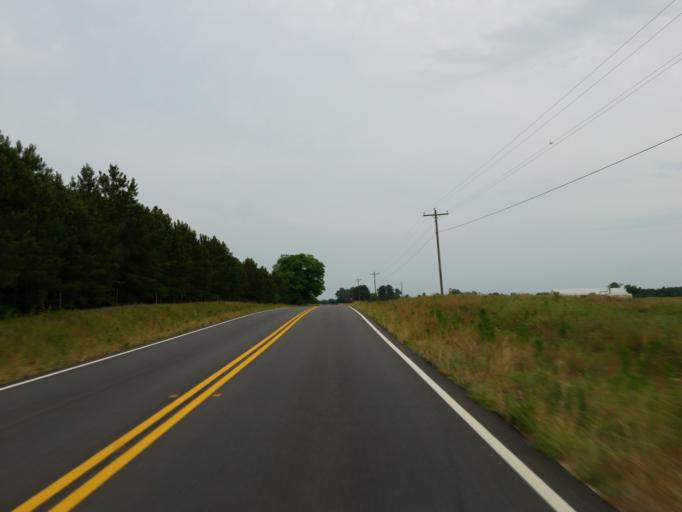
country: US
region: Georgia
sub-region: Dooly County
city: Unadilla
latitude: 32.2860
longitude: -83.7484
